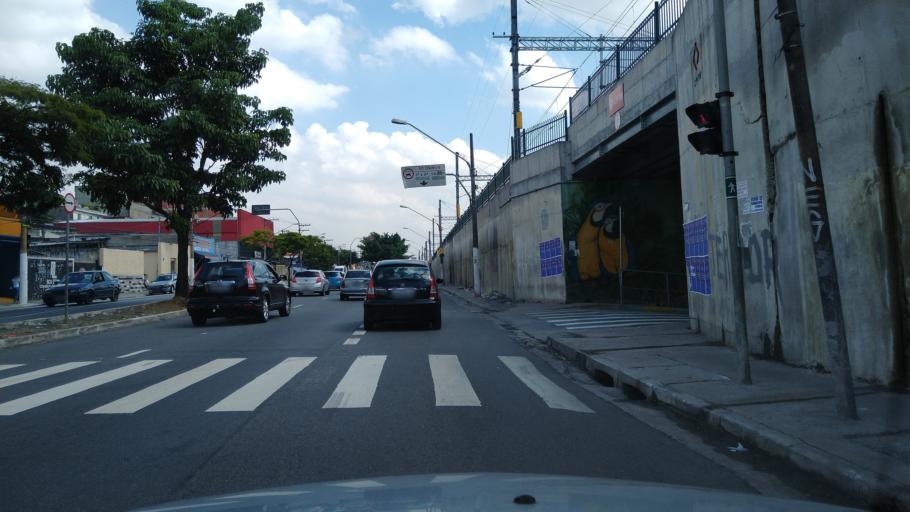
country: BR
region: Sao Paulo
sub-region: Guarulhos
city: Guarulhos
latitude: -23.5025
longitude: -46.5350
